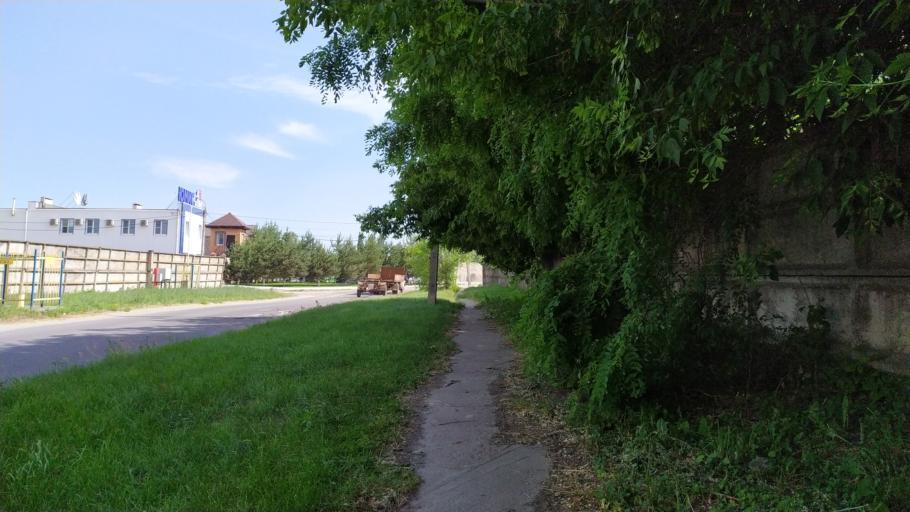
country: RU
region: Kursk
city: Kursk
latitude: 51.6592
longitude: 36.1529
